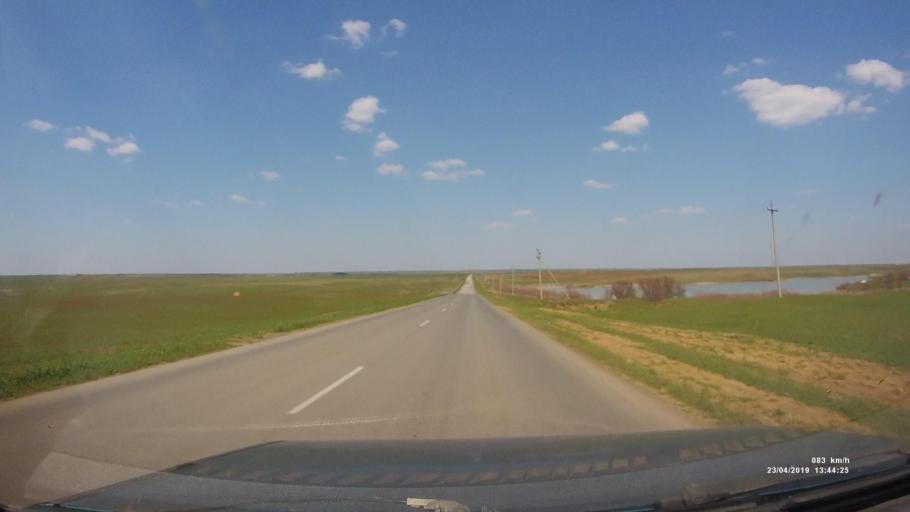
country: RU
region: Kalmykiya
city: Yashalta
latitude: 46.5808
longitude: 42.8161
